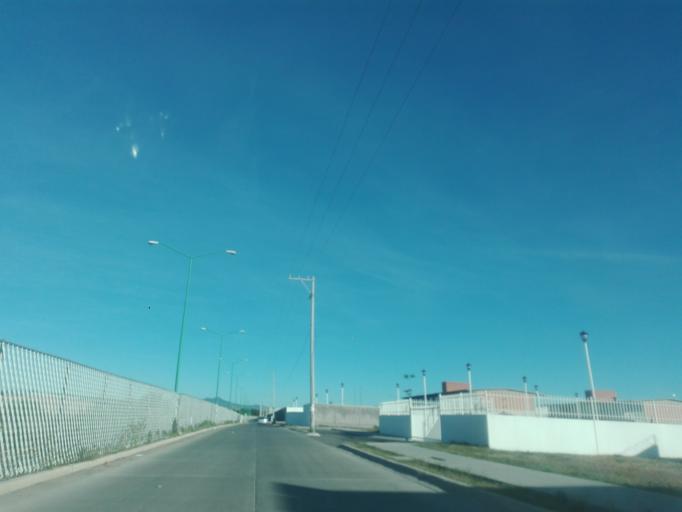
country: MX
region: Guanajuato
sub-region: Leon
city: Ladrilleras del Refugio
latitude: 21.0735
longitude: -101.5651
